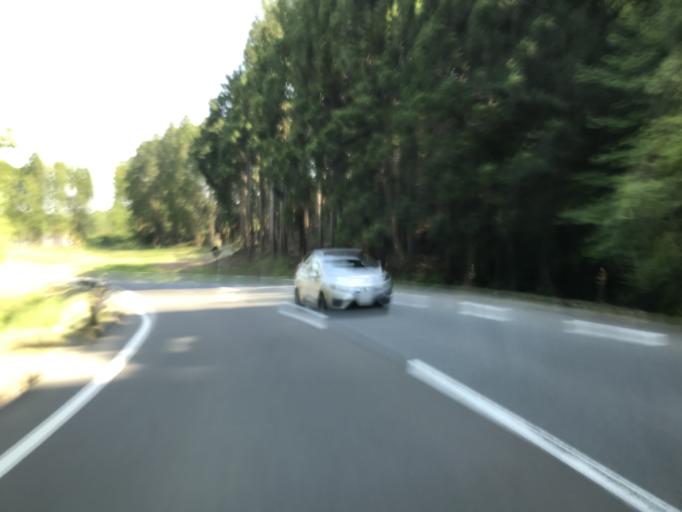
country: JP
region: Miyagi
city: Marumori
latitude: 37.7930
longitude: 140.8823
